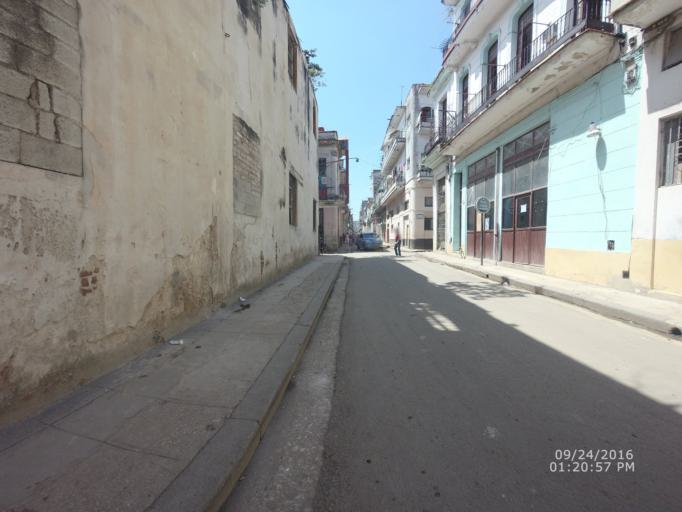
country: CU
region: La Habana
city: La Habana Vieja
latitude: 23.1342
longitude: -82.3514
